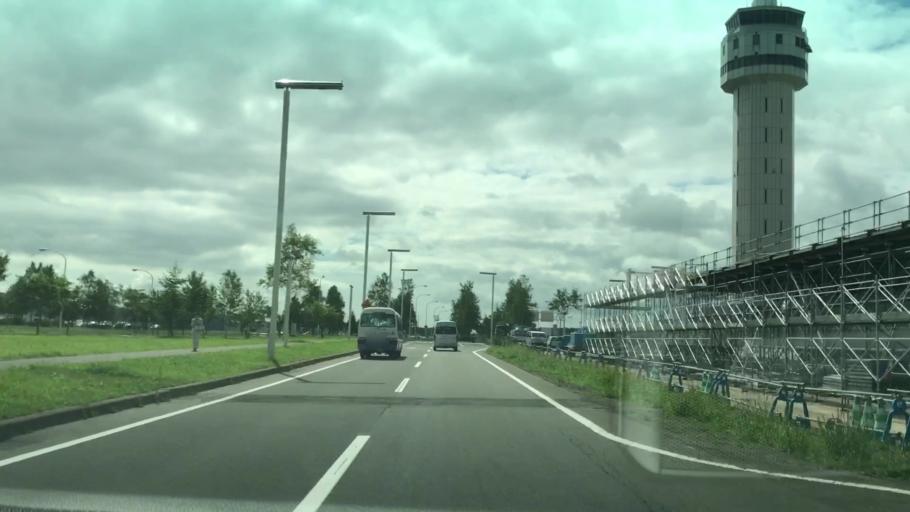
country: JP
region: Hokkaido
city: Chitose
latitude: 42.7846
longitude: 141.6773
